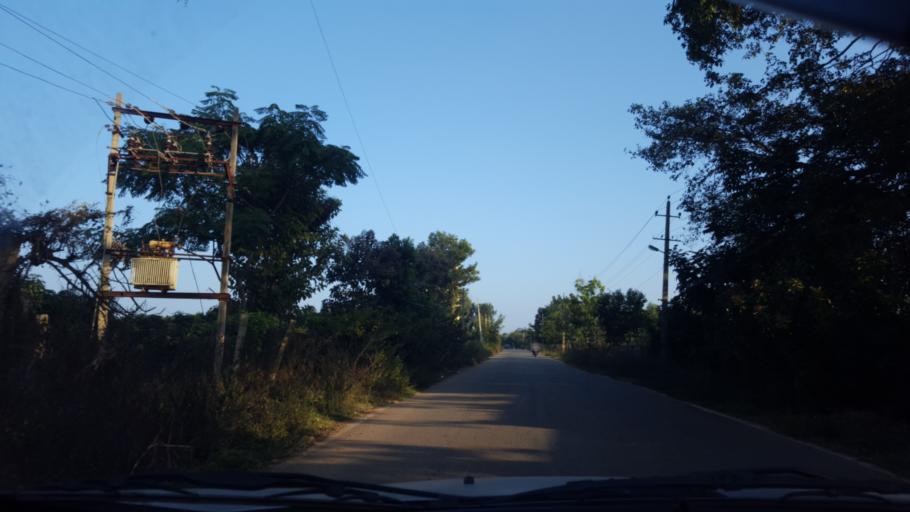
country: IN
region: Karnataka
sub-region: Bangalore Urban
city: Yelahanka
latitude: 13.1734
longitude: 77.5962
